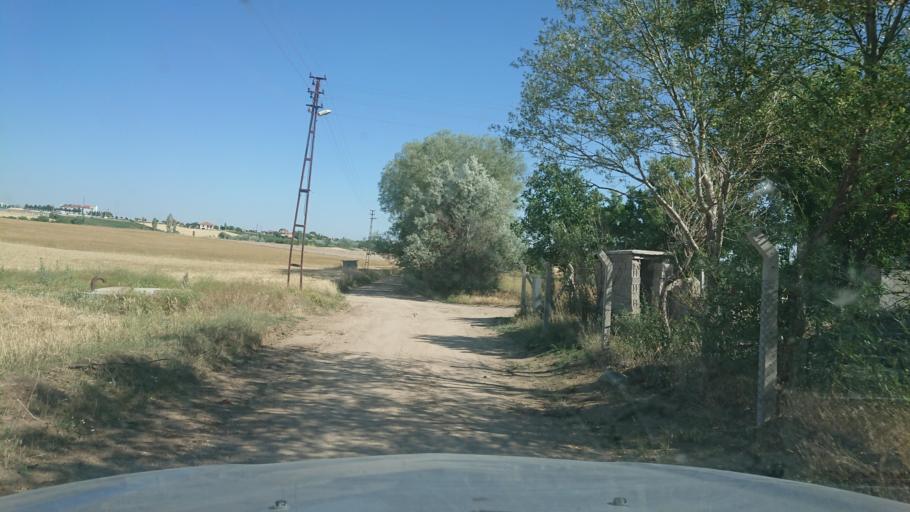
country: TR
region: Aksaray
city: Agacoren
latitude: 38.8574
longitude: 33.9127
